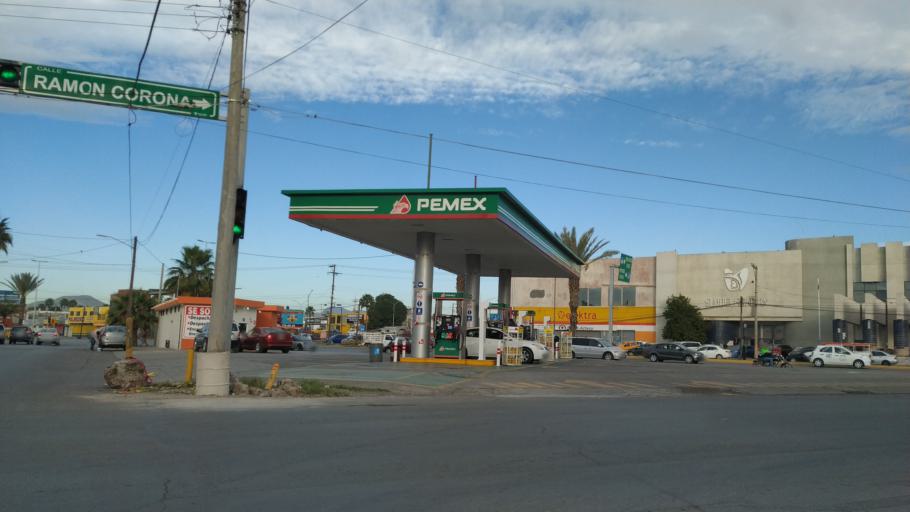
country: MX
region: Coahuila
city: Torreon
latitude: 25.5442
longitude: -103.4536
